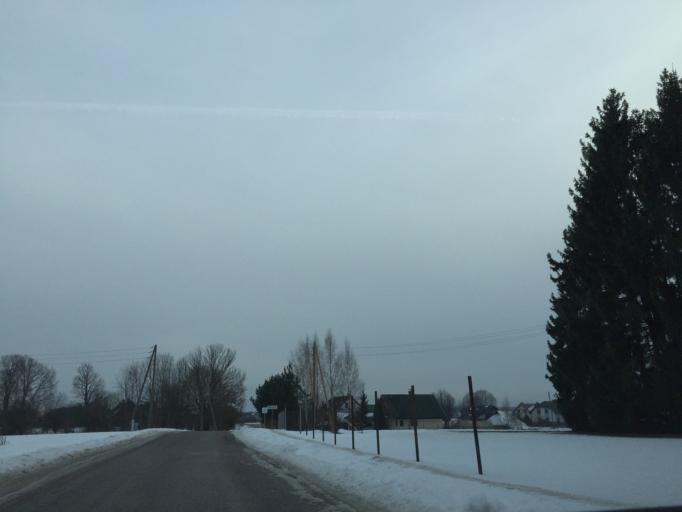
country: LV
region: Ikskile
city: Ikskile
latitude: 56.8423
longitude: 24.4722
